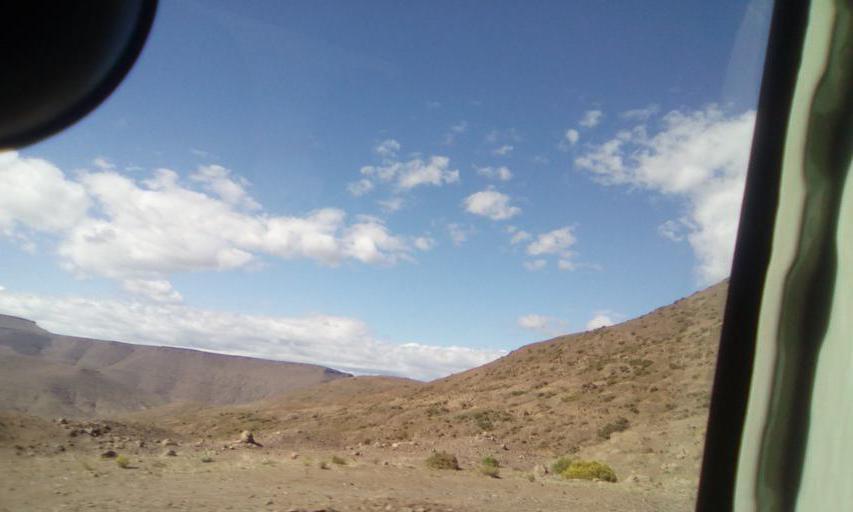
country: LS
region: Qacha's Nek
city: Qacha's Nek
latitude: -30.0098
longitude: 28.1750
